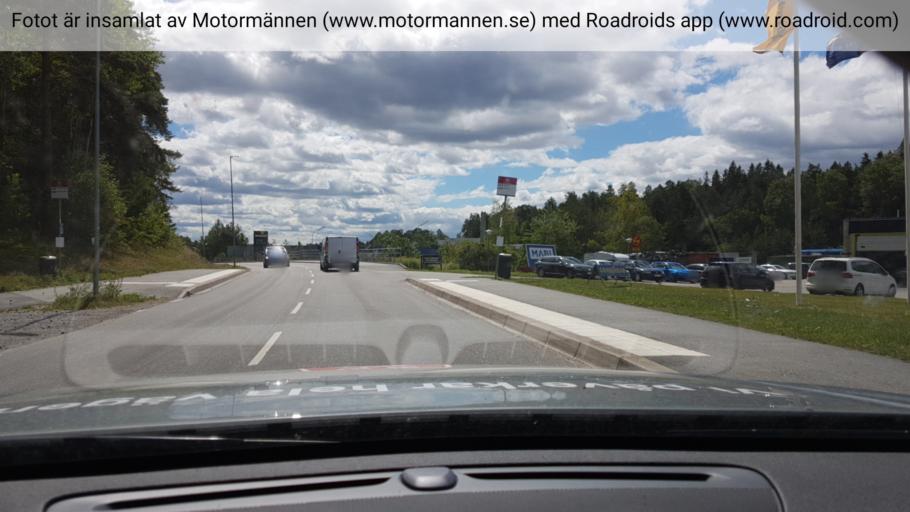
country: SE
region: Stockholm
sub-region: Jarfalla Kommun
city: Jakobsberg
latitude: 59.4061
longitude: 17.8437
